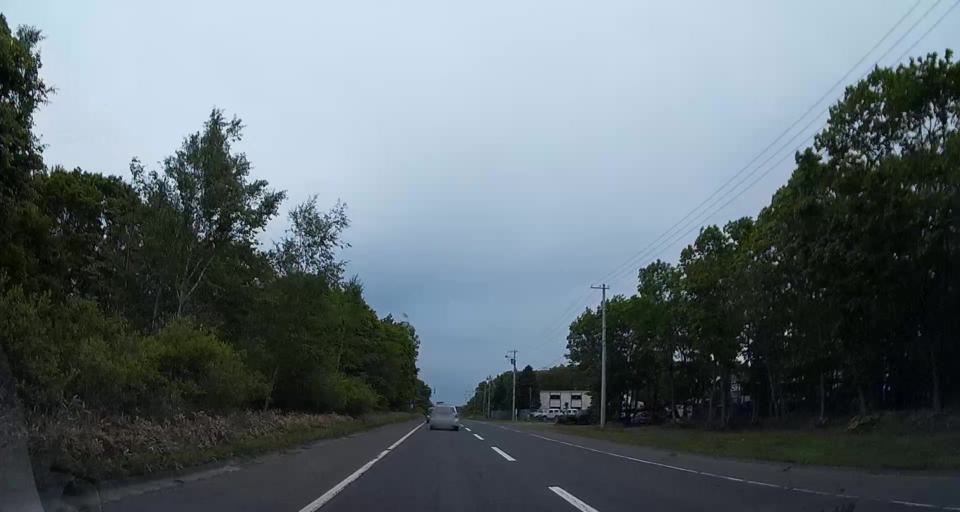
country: JP
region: Hokkaido
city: Tomakomai
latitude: 42.6963
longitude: 141.7376
